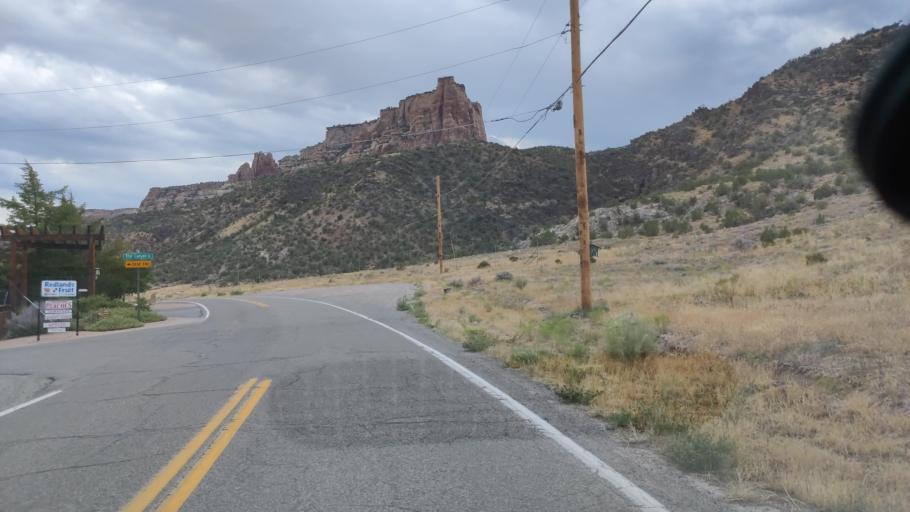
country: US
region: Colorado
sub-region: Mesa County
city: Redlands
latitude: 39.0930
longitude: -108.6920
